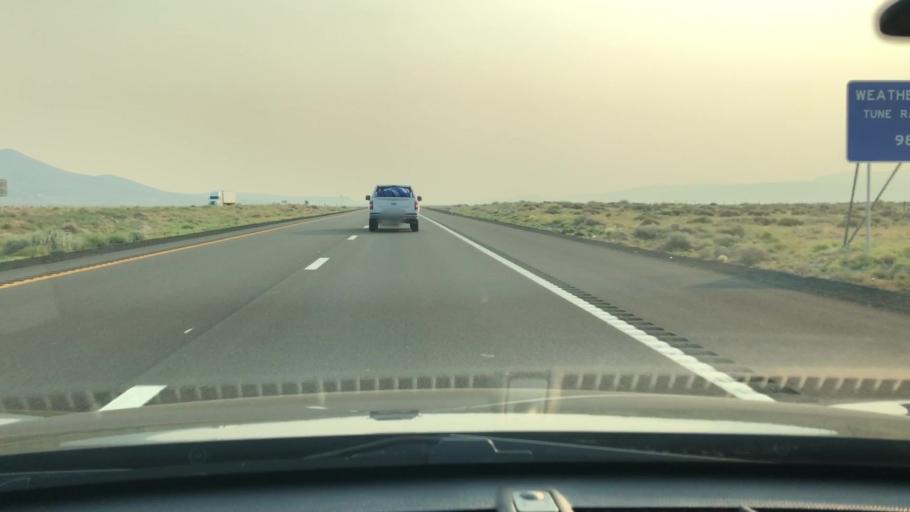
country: US
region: Nevada
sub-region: Lyon County
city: Fernley
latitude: 39.6368
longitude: -119.1822
